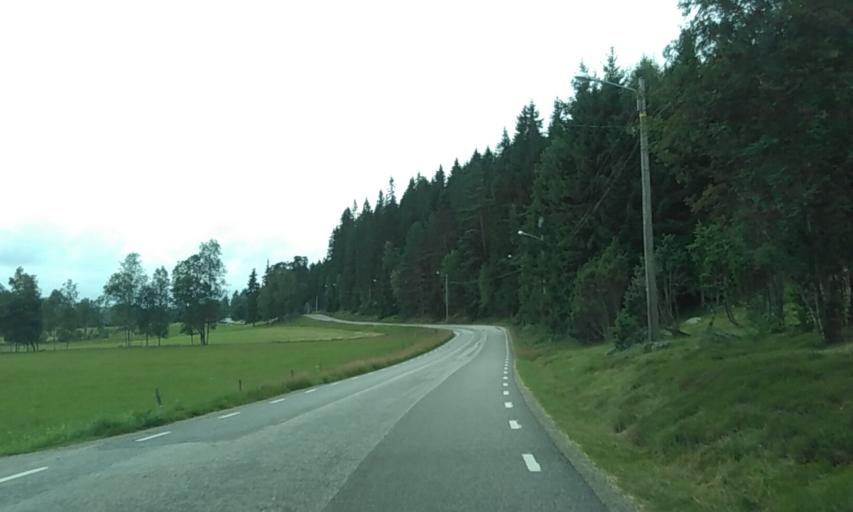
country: SE
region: Vaestra Goetaland
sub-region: Bollebygds Kommun
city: Bollebygd
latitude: 57.8007
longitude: 12.6312
